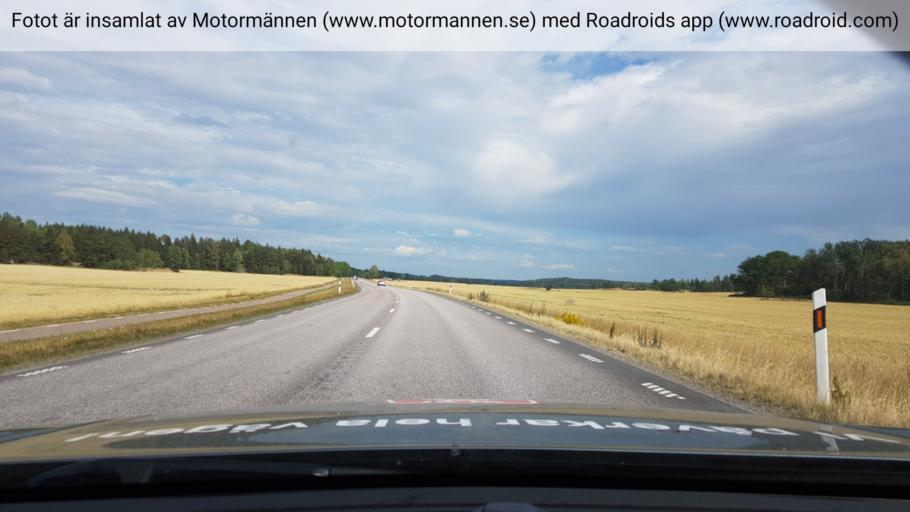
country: SE
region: Uppsala
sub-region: Uppsala Kommun
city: Uppsala
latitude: 59.8510
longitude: 17.4569
